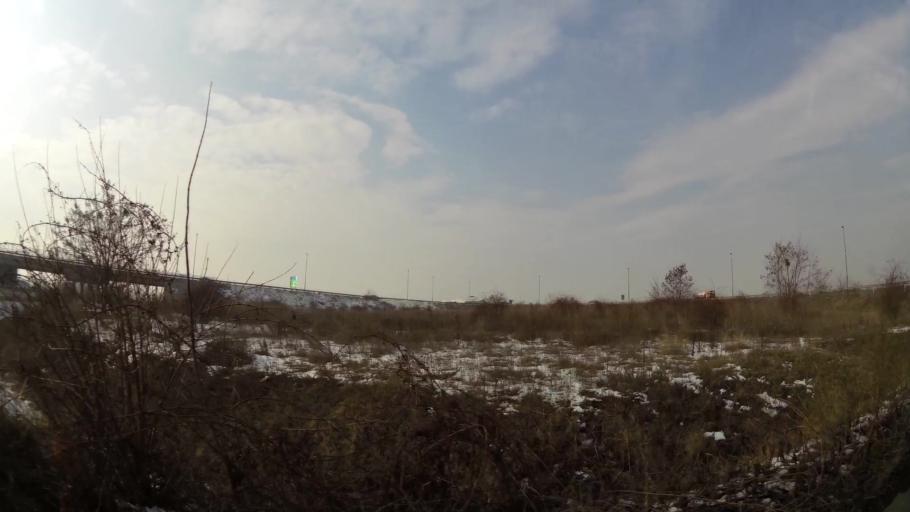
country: MK
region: Suto Orizari
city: Suto Orizare
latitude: 42.0535
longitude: 21.3831
